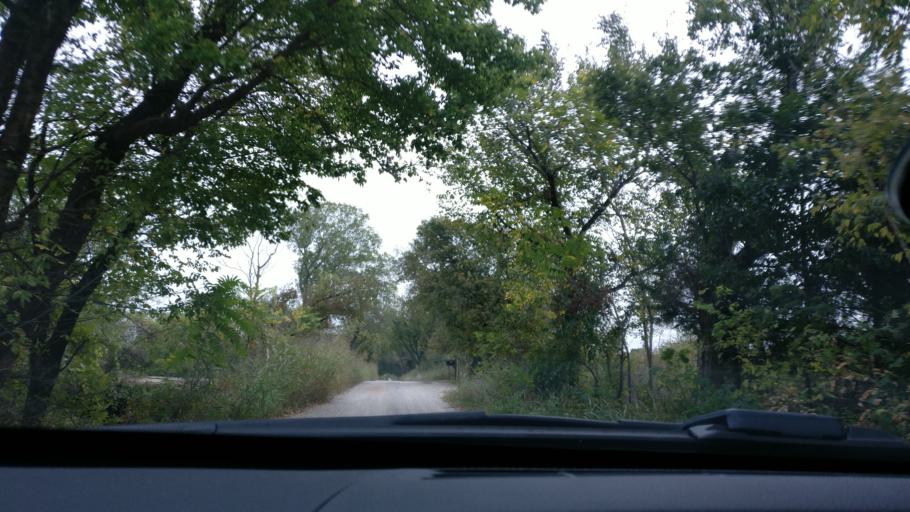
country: US
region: Oklahoma
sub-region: McClain County
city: Goldsby
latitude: 35.1896
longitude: -97.5348
